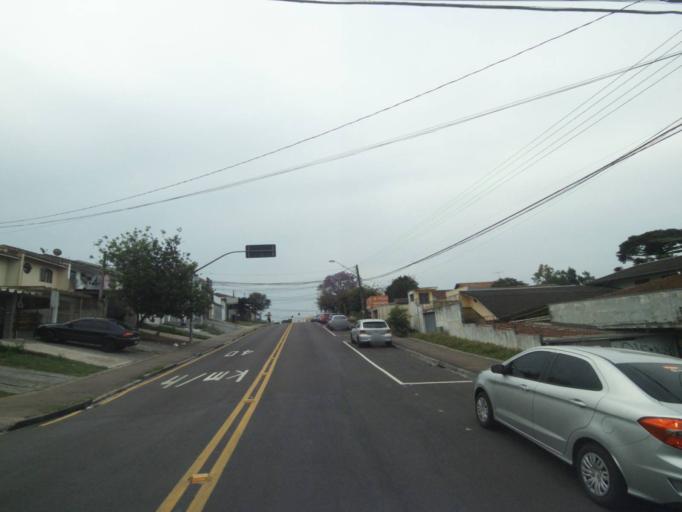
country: BR
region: Parana
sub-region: Pinhais
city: Pinhais
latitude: -25.4086
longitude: -49.2082
